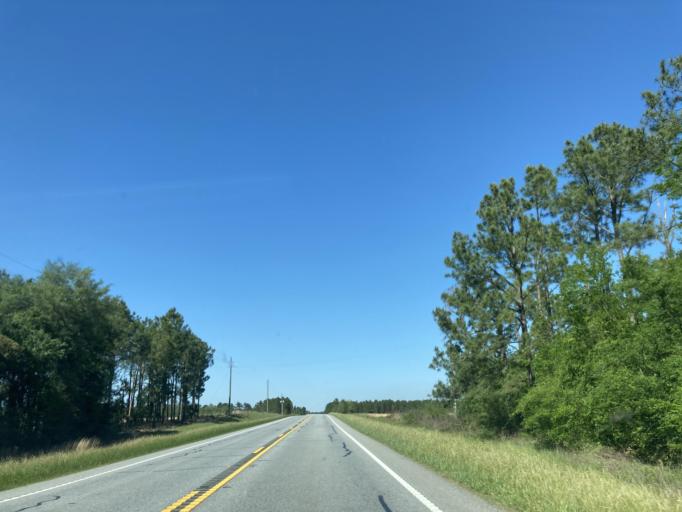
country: US
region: Georgia
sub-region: Baker County
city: Newton
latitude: 31.2351
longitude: -84.4382
